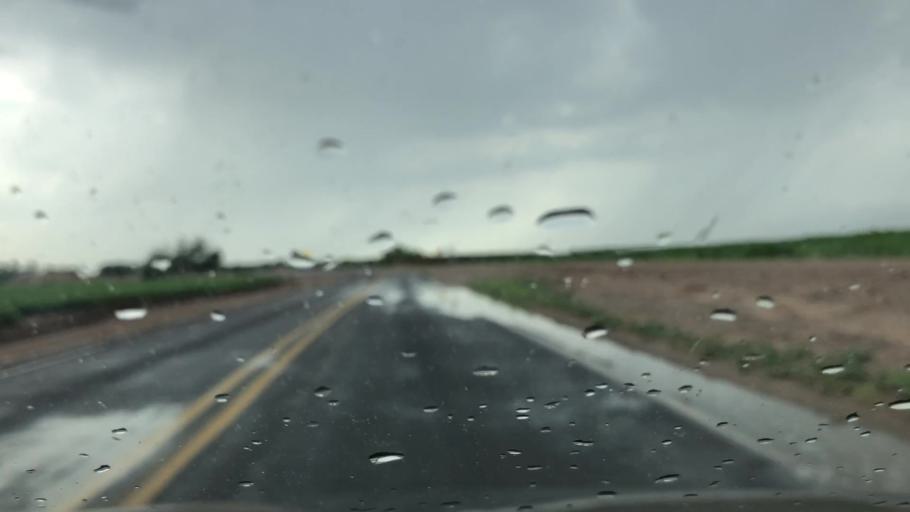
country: US
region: New Mexico
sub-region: Dona Ana County
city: Vado
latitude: 32.0665
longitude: -106.6794
